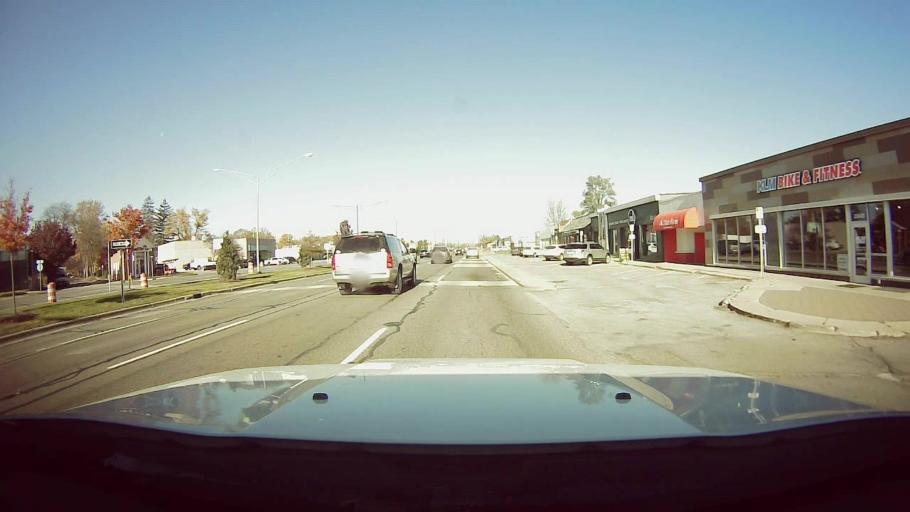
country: US
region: Michigan
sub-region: Oakland County
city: Birmingham
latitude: 42.5359
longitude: -83.2033
